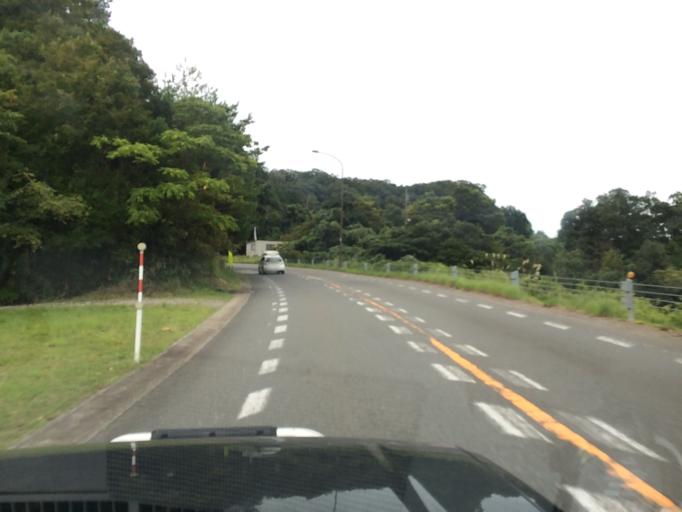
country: JP
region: Hyogo
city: Toyooka
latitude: 35.5129
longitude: 134.7903
